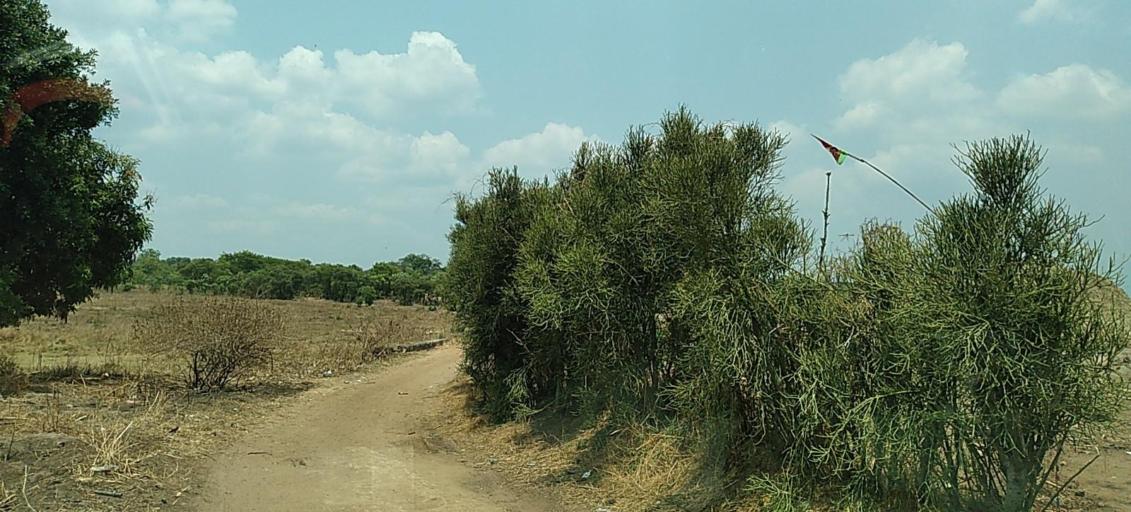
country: ZM
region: Copperbelt
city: Luanshya
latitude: -13.1211
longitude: 28.3073
